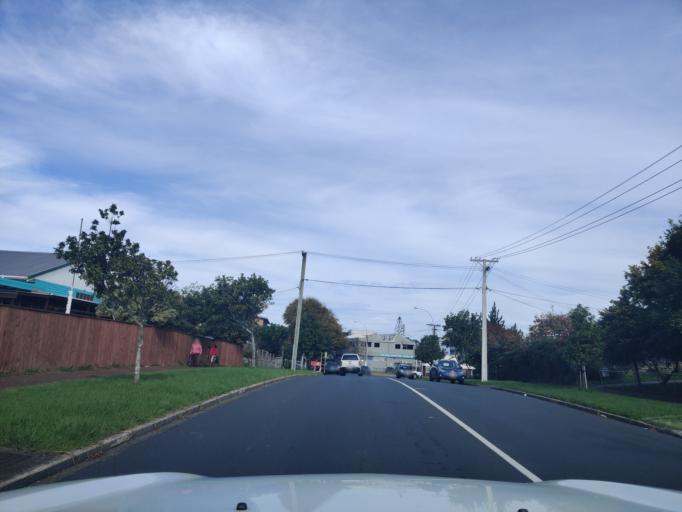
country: NZ
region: Auckland
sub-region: Auckland
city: Tamaki
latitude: -36.8999
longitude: 174.8584
